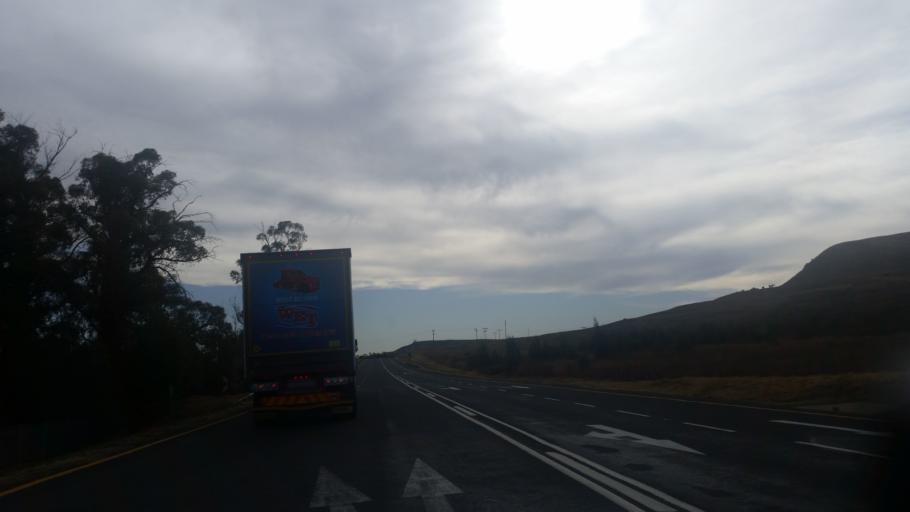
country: ZA
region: Orange Free State
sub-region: Thabo Mofutsanyana District Municipality
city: Phuthaditjhaba
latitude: -28.3132
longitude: 28.7280
